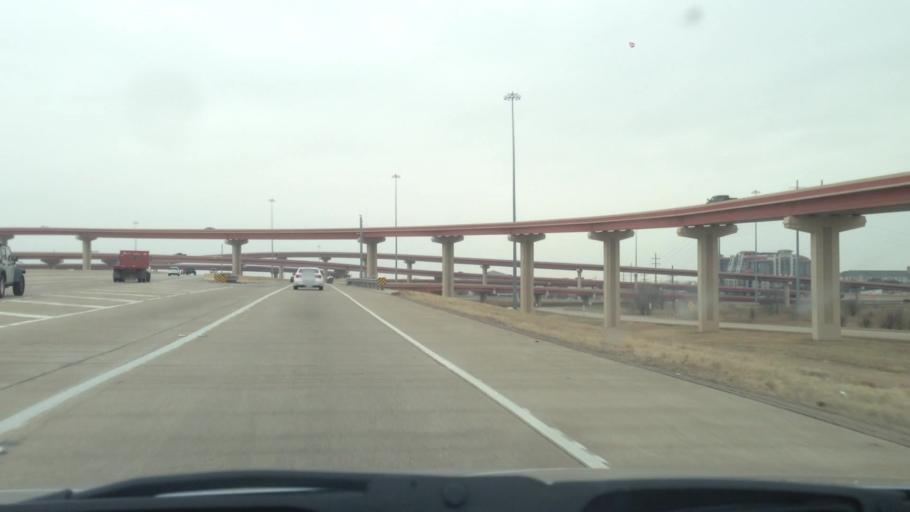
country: US
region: Texas
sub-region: Tarrant County
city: Euless
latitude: 32.8414
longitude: -97.0171
